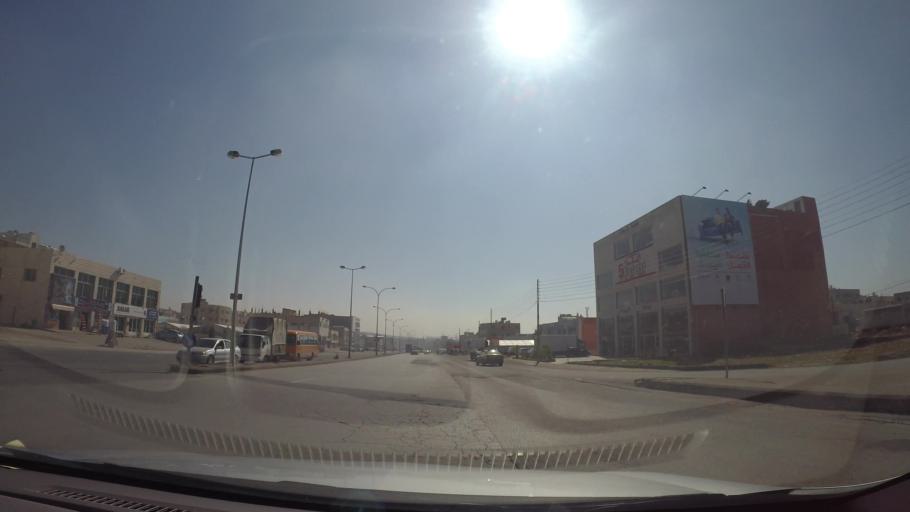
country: JO
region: Amman
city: Al Bunayyat ash Shamaliyah
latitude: 31.8998
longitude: 35.8956
